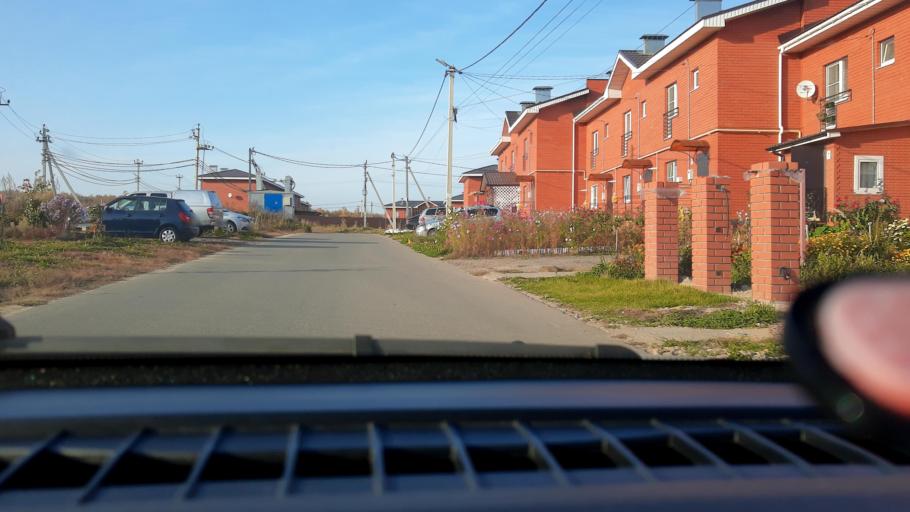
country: RU
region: Nizjnij Novgorod
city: Afonino
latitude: 56.2151
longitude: 44.0843
